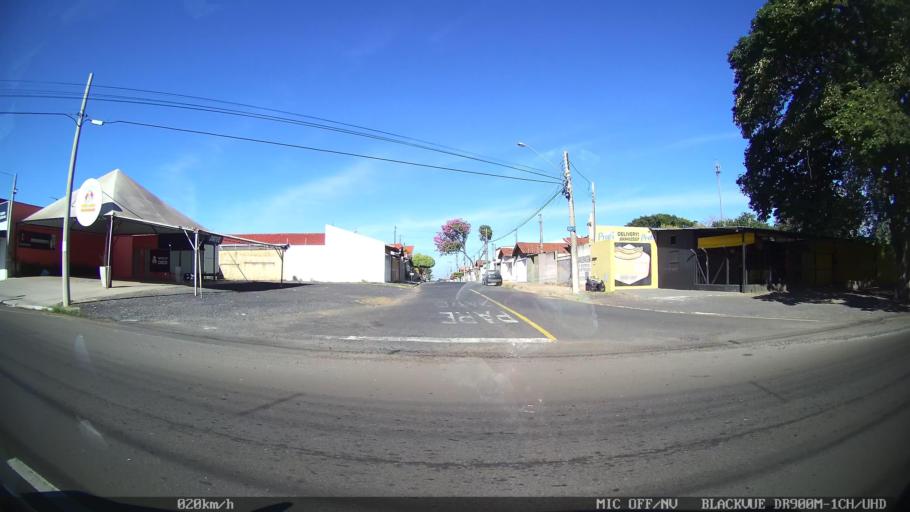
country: BR
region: Sao Paulo
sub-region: Franca
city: Franca
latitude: -20.5616
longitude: -47.3704
